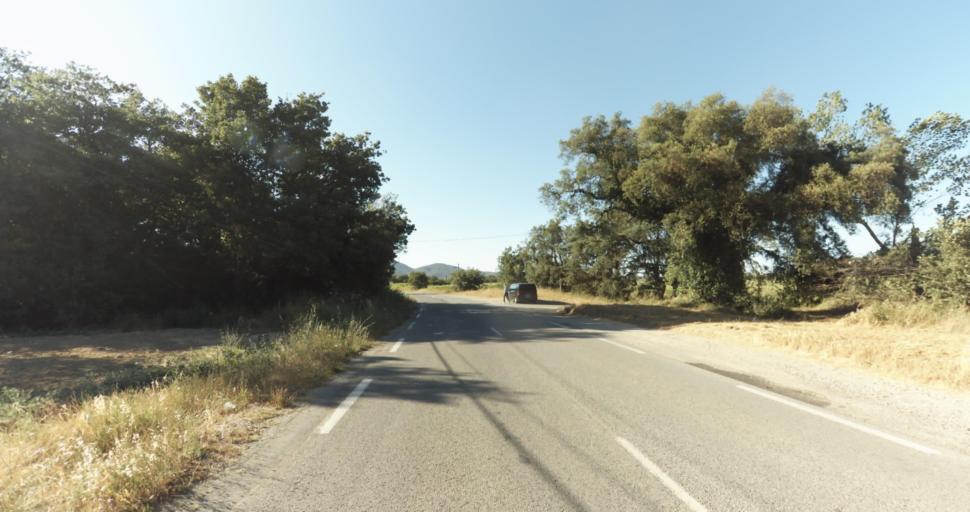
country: FR
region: Provence-Alpes-Cote d'Azur
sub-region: Departement du Var
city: Gassin
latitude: 43.2476
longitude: 6.5940
